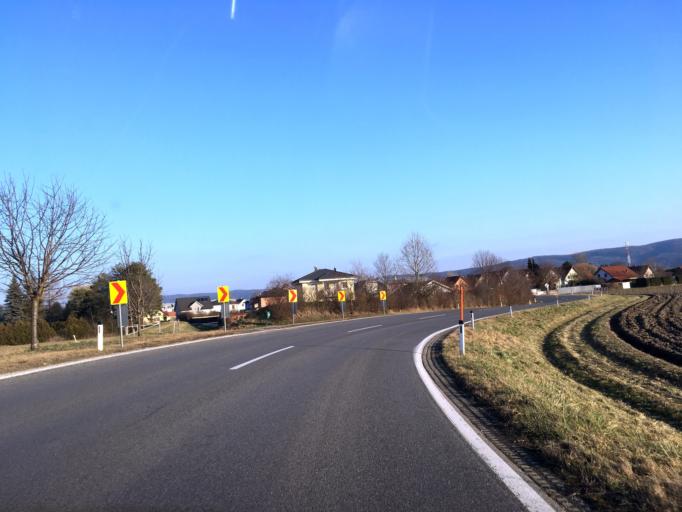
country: AT
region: Lower Austria
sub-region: Politischer Bezirk Tulln
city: Konigstetten
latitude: 48.3311
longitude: 16.1444
